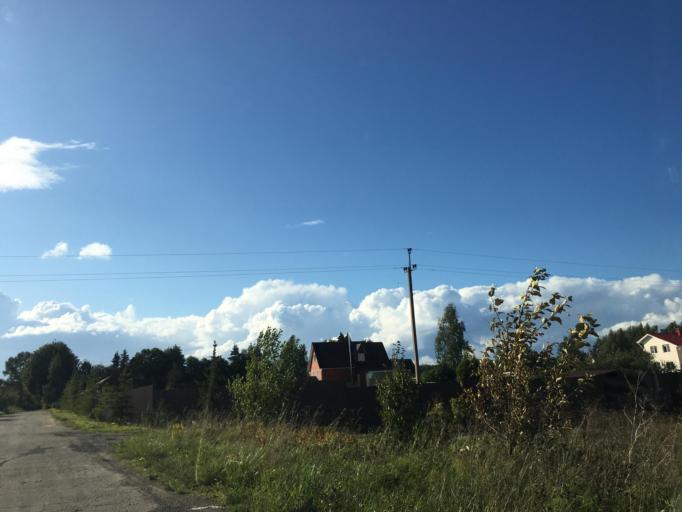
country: RU
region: Pskov
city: Izborsk
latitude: 57.7700
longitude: 27.9817
